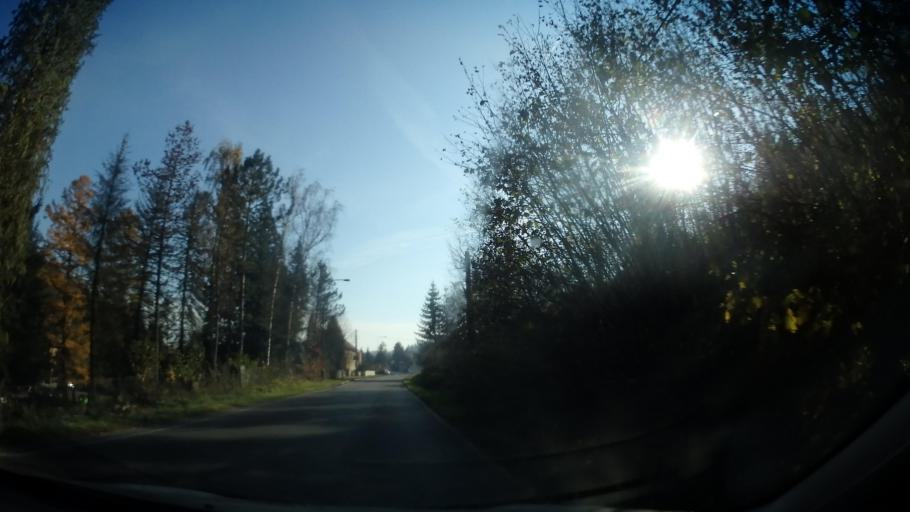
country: CZ
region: Central Bohemia
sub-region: Okres Praha-Vychod
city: Mnichovice
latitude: 49.9433
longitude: 14.7015
